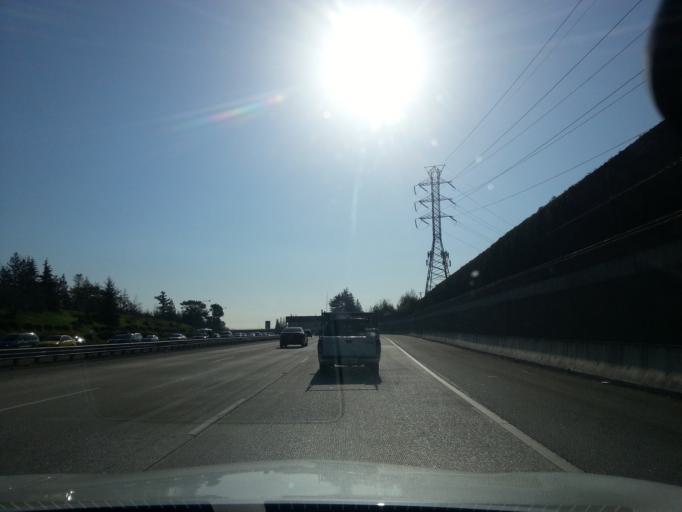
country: US
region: California
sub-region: Santa Clara County
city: Monte Sereno
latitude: 37.2609
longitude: -121.9718
